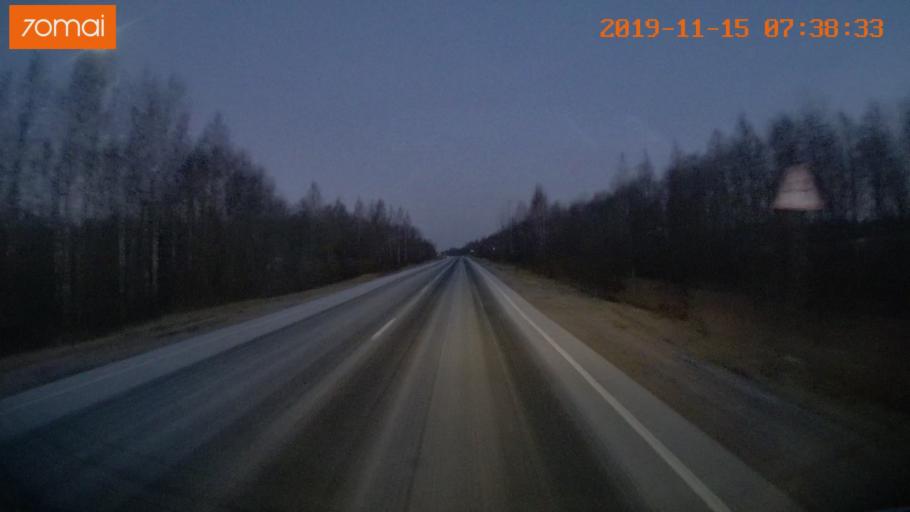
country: RU
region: Vologda
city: Sheksna
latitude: 58.7584
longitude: 38.3995
